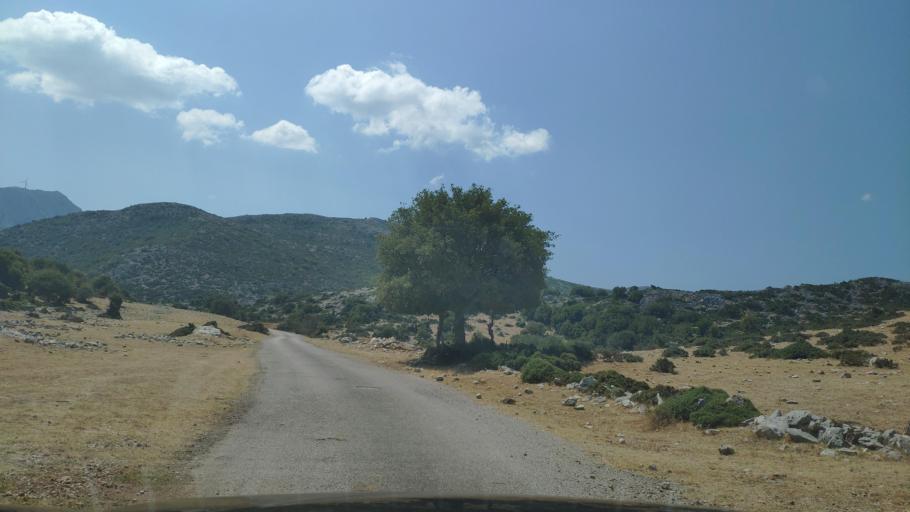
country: GR
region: West Greece
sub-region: Nomos Aitolias kai Akarnanias
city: Monastirakion
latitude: 38.8015
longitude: 20.9478
